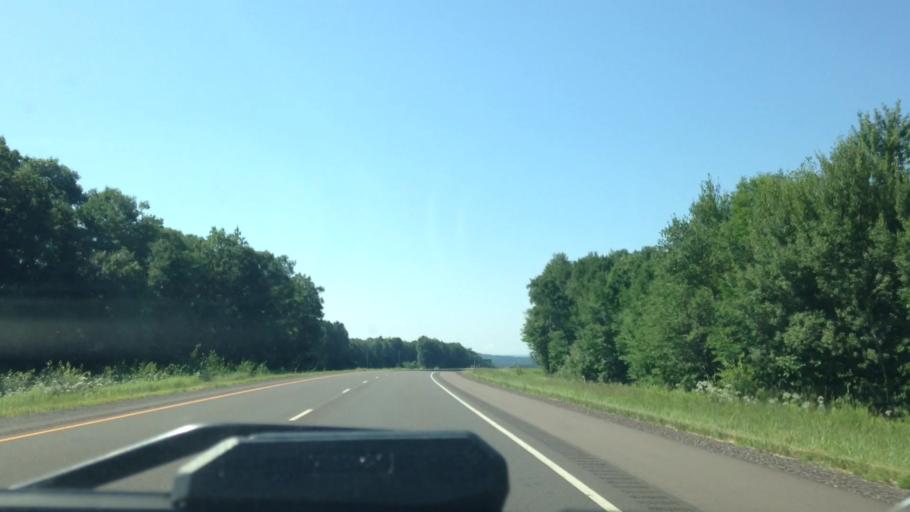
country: US
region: Wisconsin
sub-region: Washburn County
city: Spooner
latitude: 45.9402
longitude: -91.8285
